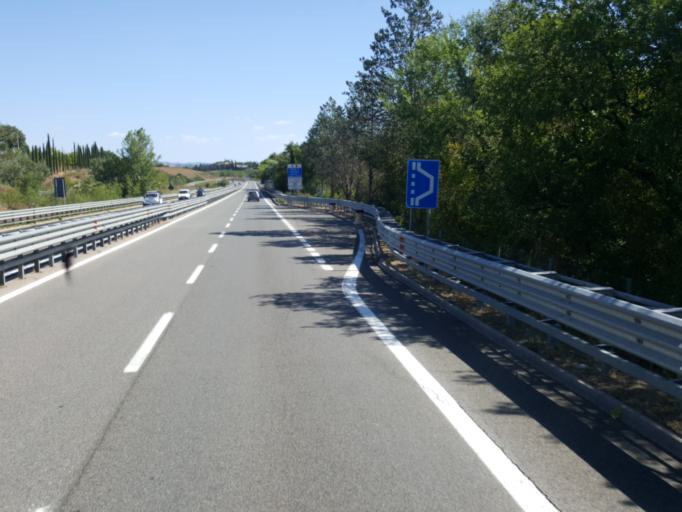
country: IT
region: Tuscany
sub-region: Provincia di Grosseto
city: Campagnatico
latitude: 42.9080
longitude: 11.2477
